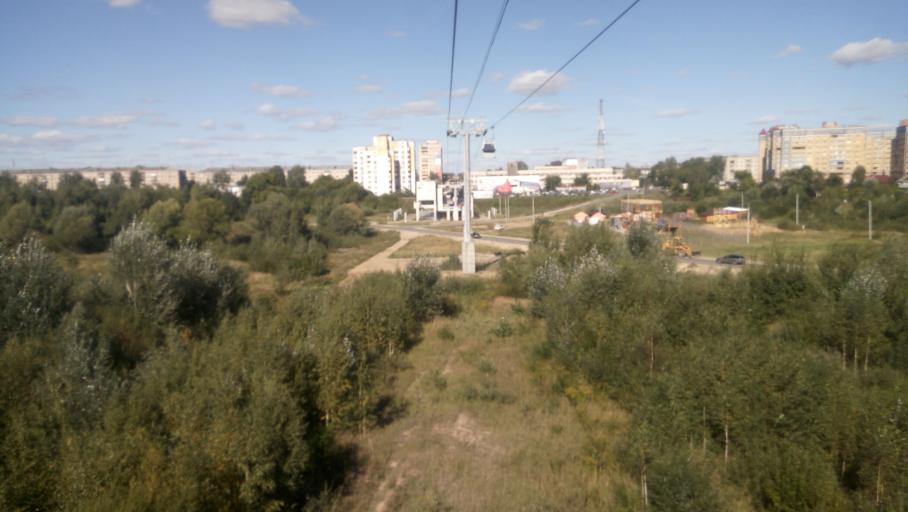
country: RU
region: Nizjnij Novgorod
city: Bor
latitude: 56.3518
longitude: 44.0595
